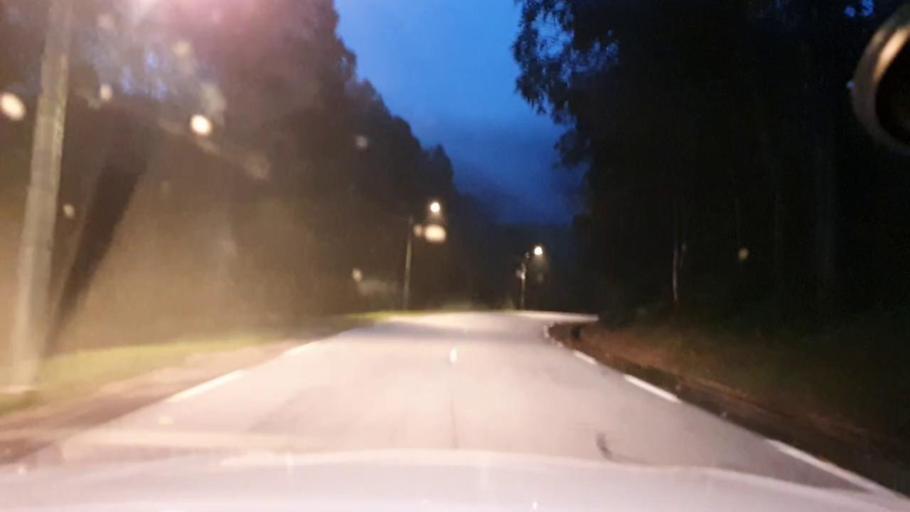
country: RW
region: Southern Province
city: Nzega
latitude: -2.5304
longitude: 29.3934
